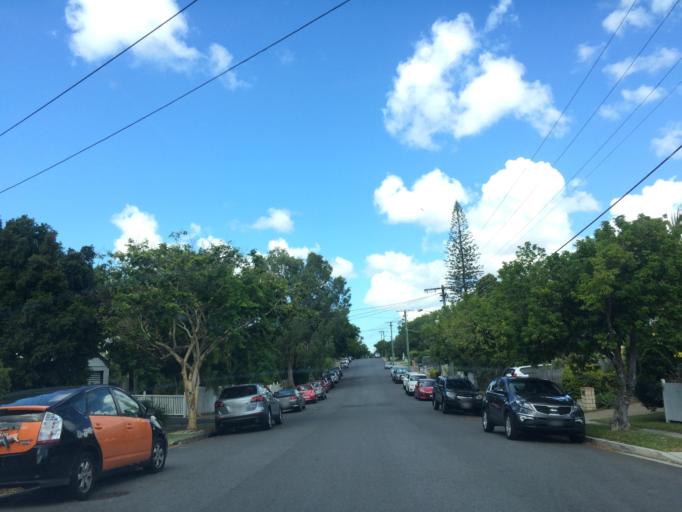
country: AU
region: Queensland
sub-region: Brisbane
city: Woolloongabba
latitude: -27.4852
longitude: 153.0473
